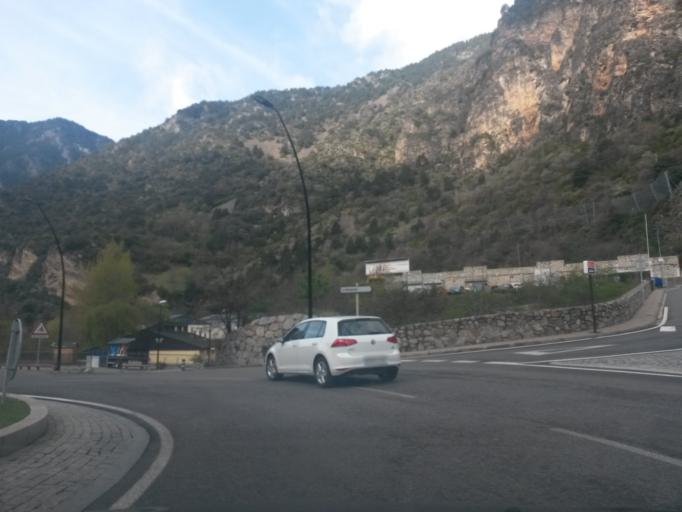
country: AD
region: Sant Julia de Loria
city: Sant Julia de Loria
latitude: 42.4845
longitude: 1.4912
